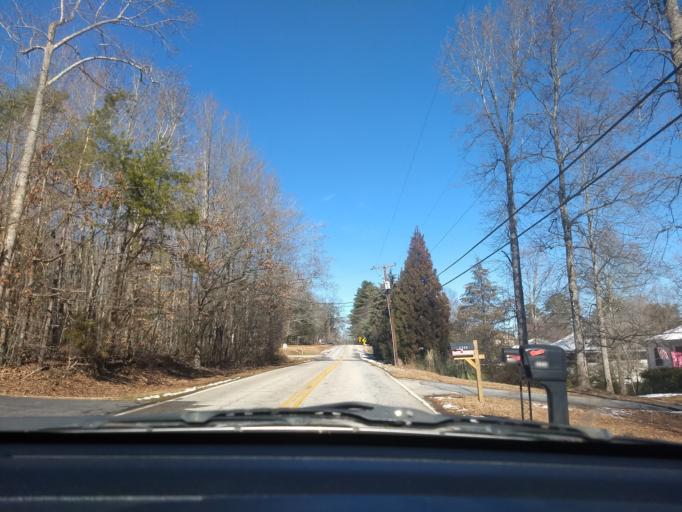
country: US
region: South Carolina
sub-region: Greenville County
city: Wade Hampton
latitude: 34.9236
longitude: -82.3664
